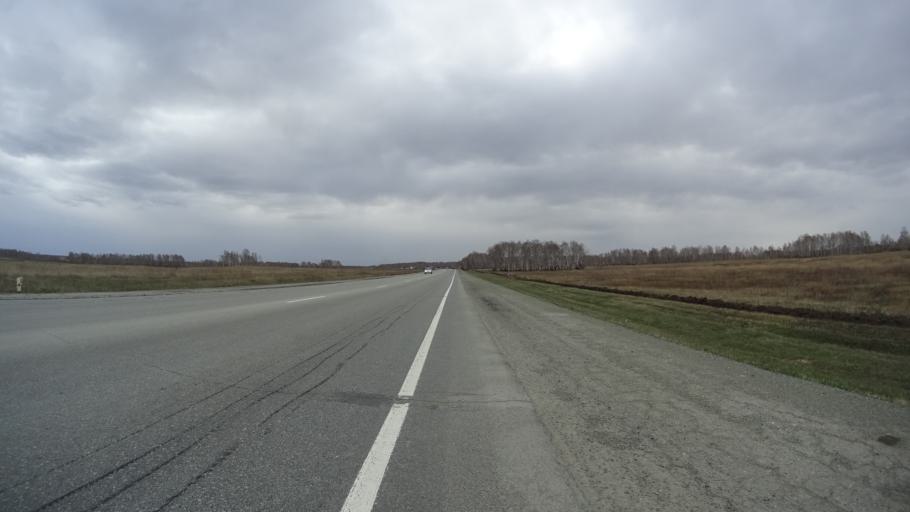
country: RU
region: Chelyabinsk
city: Yemanzhelinsk
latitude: 54.7017
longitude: 61.2534
